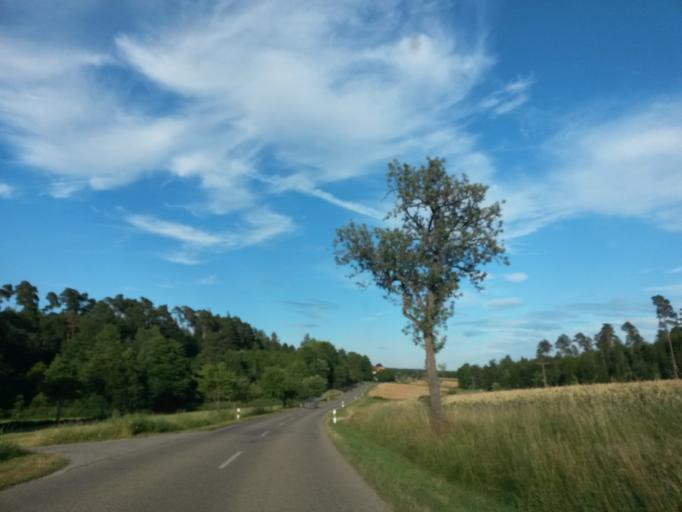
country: DE
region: Baden-Wuerttemberg
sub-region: Regierungsbezirk Stuttgart
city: Ellenberg
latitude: 49.0531
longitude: 10.2122
